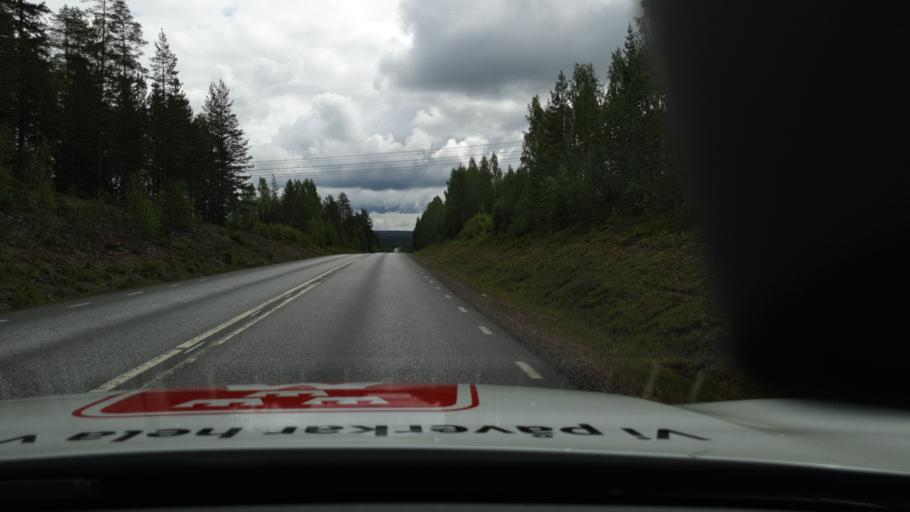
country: SE
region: Norrbotten
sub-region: Pitea Kommun
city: Norrfjarden
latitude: 65.6159
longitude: 21.4332
